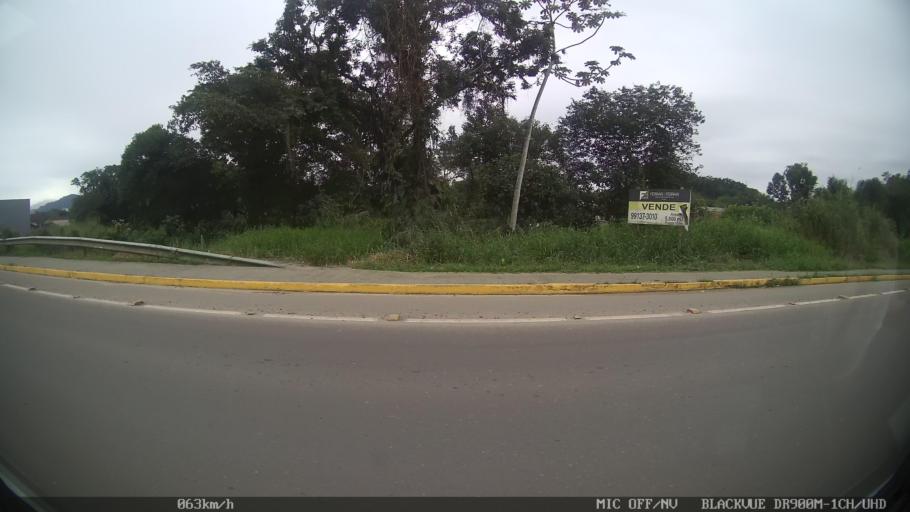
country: BR
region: Santa Catarina
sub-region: Joinville
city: Joinville
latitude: -26.2920
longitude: -48.8956
